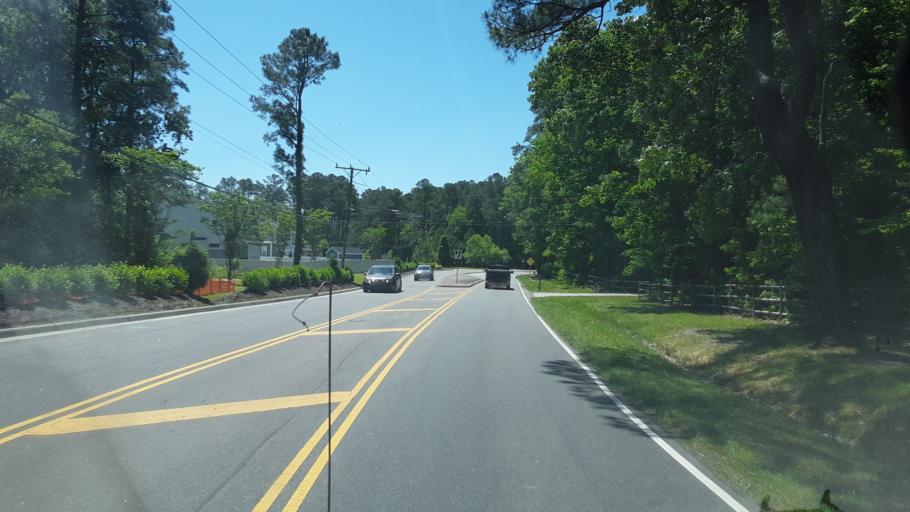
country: US
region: Virginia
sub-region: City of Virginia Beach
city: Virginia Beach
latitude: 36.7412
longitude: -75.9886
